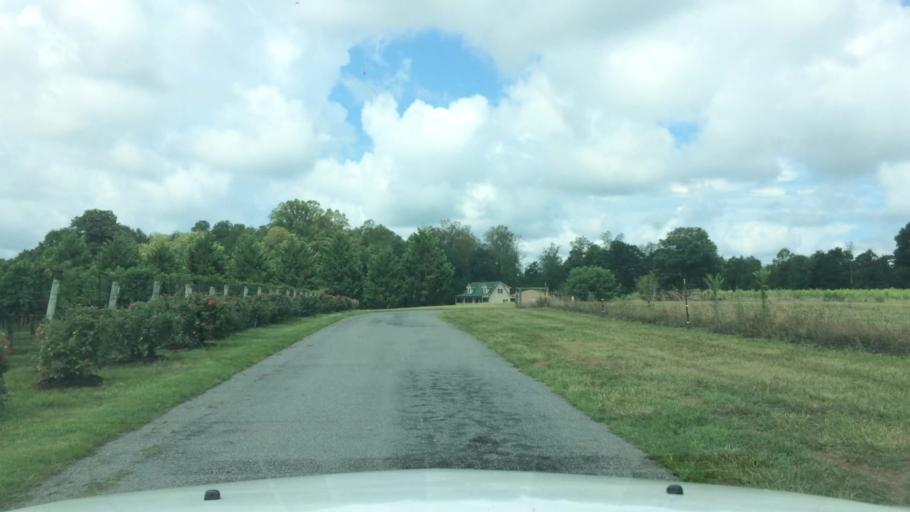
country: US
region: North Carolina
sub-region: Yadkin County
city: Jonesville
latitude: 36.0972
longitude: -80.8537
